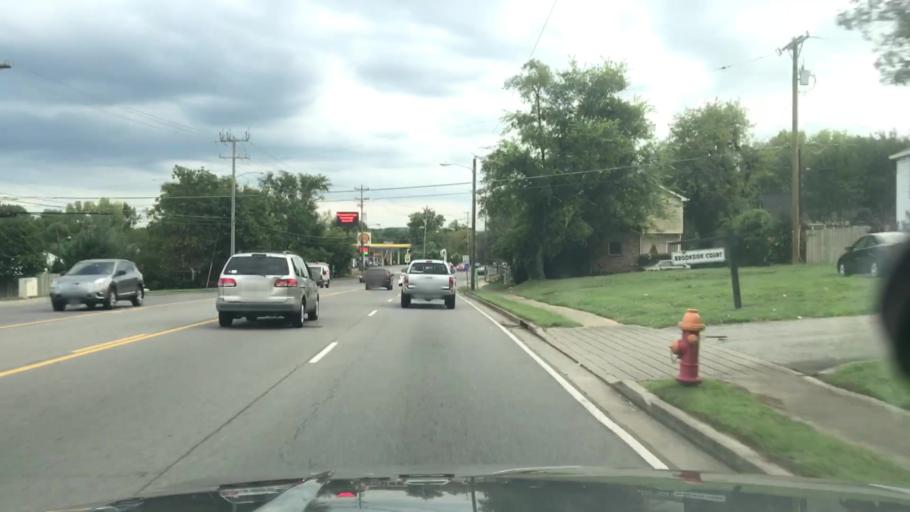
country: US
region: Tennessee
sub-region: Davidson County
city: Belle Meade
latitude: 36.1404
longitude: -86.8575
